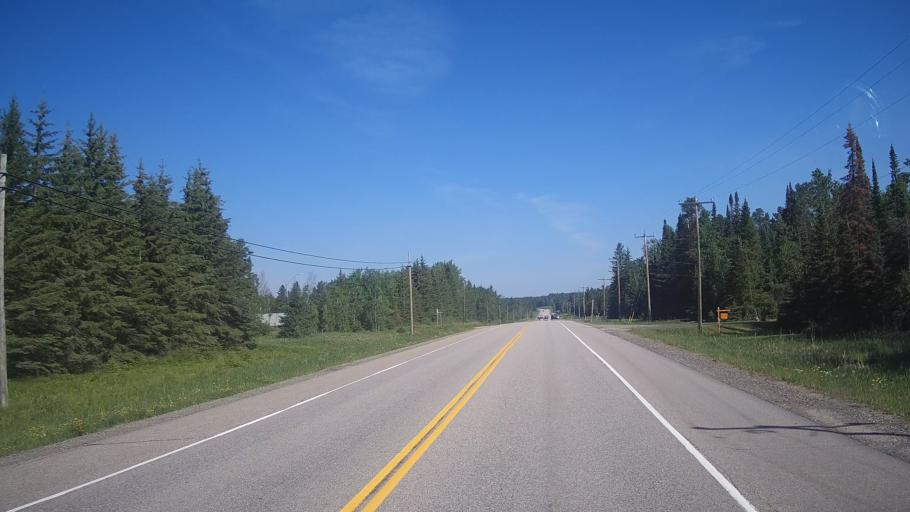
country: CA
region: Ontario
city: Dryden
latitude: 49.7726
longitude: -92.6917
